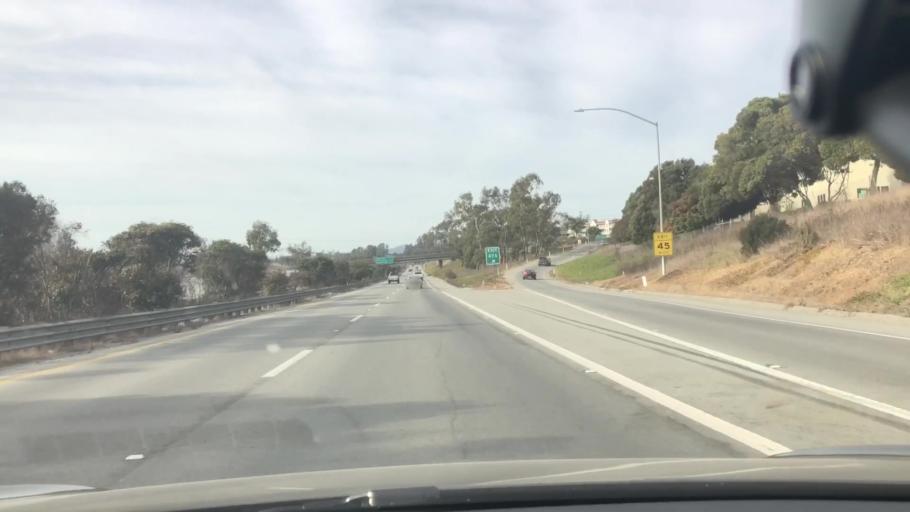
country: US
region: California
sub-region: Santa Cruz County
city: Freedom
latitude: 36.9119
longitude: -121.7852
